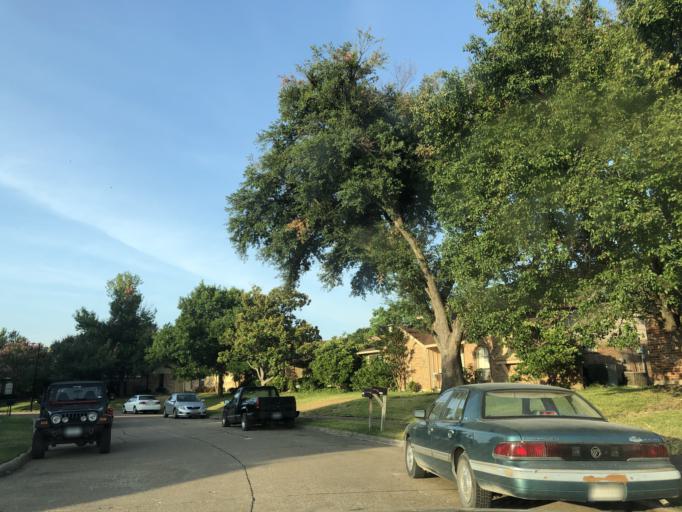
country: US
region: Texas
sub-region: Dallas County
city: Garland
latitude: 32.8562
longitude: -96.6262
